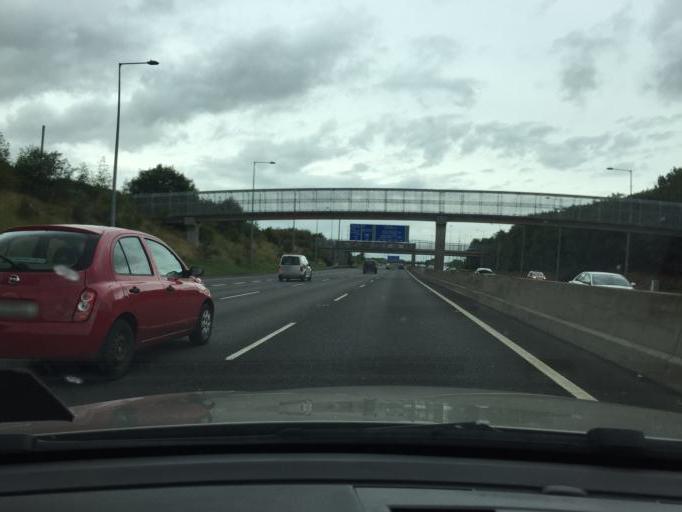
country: IE
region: Leinster
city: Firhouse
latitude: 53.3037
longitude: -6.3472
